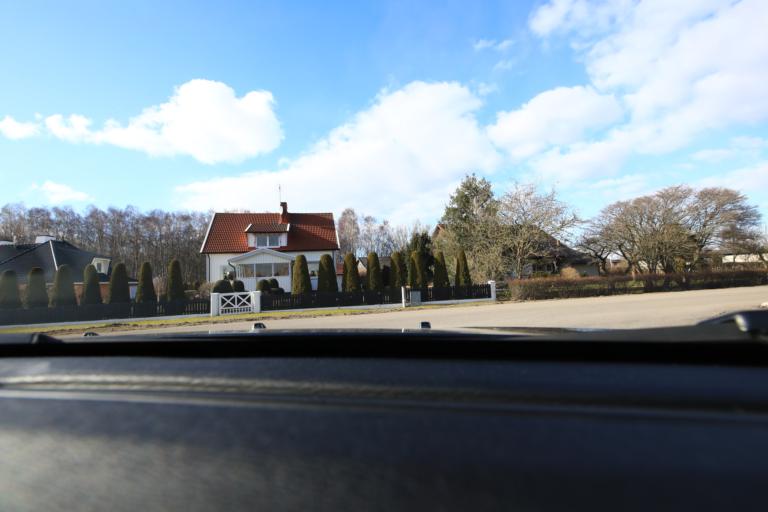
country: SE
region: Halland
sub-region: Kungsbacka Kommun
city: Frillesas
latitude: 57.2422
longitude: 12.1851
